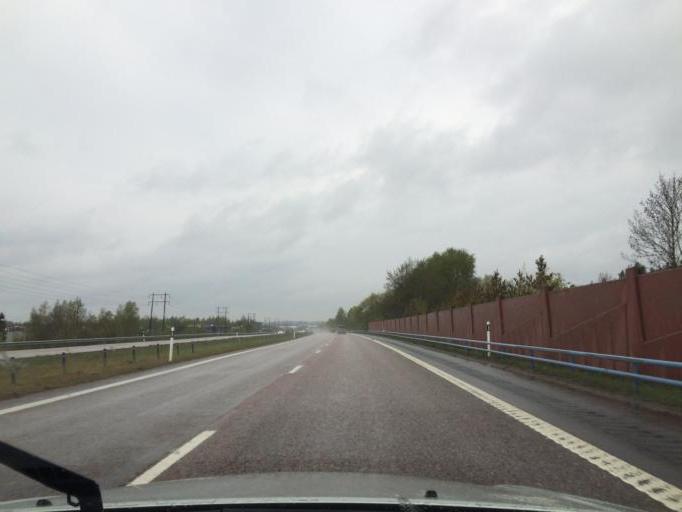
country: SE
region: Soedermanland
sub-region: Eskilstuna Kommun
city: Eskilstuna
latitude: 59.3887
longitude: 16.5091
